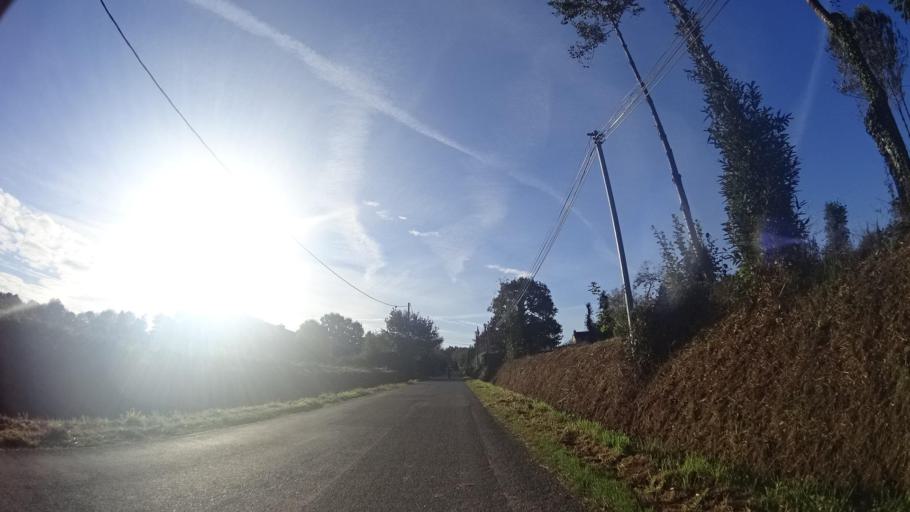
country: FR
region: Brittany
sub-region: Departement des Cotes-d'Armor
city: Evran
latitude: 48.3398
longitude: -1.9380
